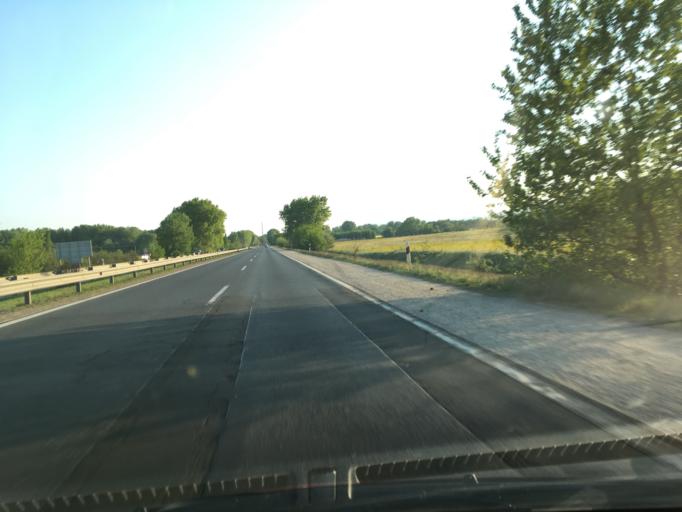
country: HU
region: Pest
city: Fot
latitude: 47.6101
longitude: 19.1618
